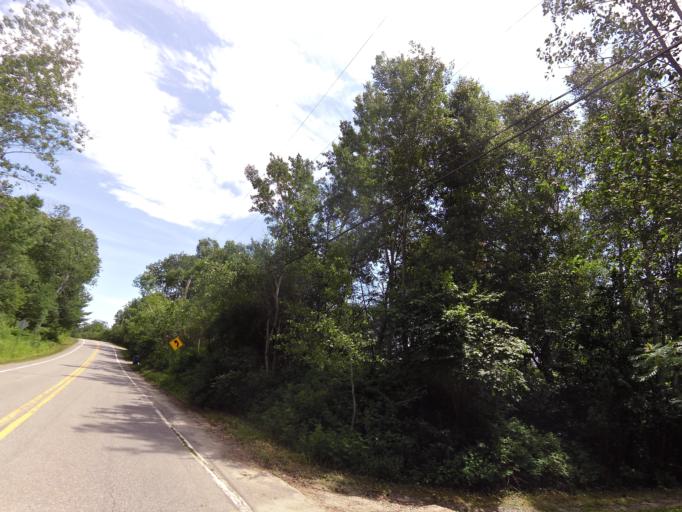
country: CA
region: Quebec
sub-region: Abitibi-Temiscamingue
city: Ville-Marie
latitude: 47.2910
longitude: -79.4500
